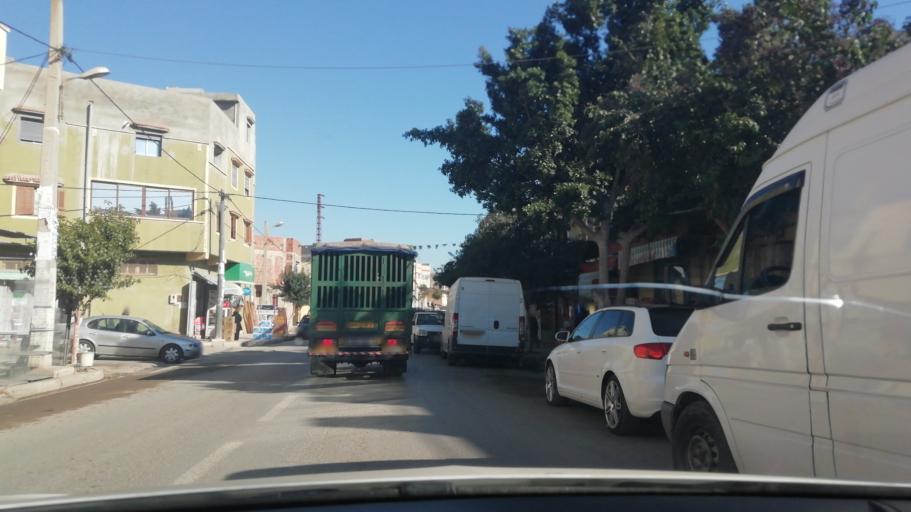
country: DZ
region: Tlemcen
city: Nedroma
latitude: 35.0451
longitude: -1.8846
